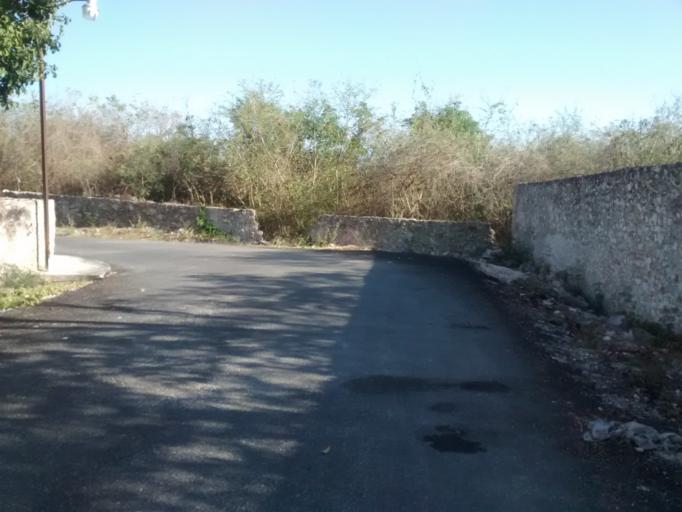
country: MX
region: Yucatan
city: Valladolid
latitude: 20.6861
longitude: -88.1872
